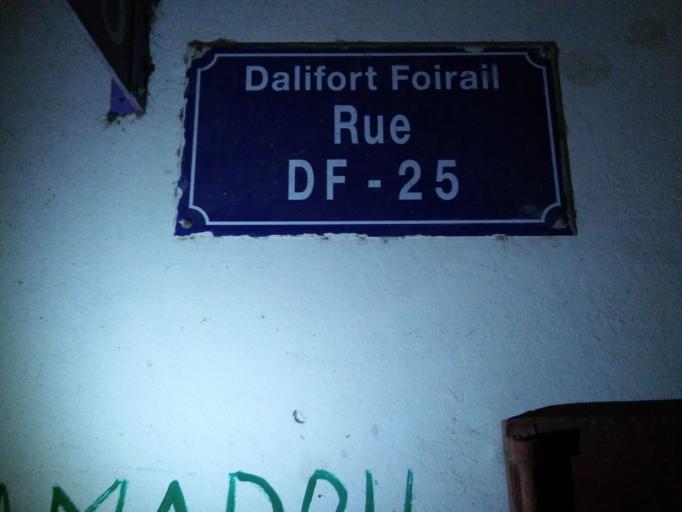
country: SN
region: Dakar
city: Pikine
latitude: 14.7437
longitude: -17.4182
